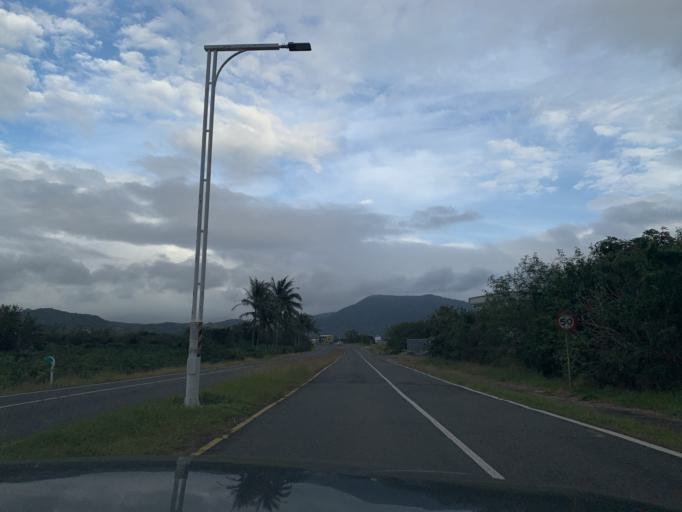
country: TW
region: Taiwan
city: Hengchun
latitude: 22.0522
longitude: 120.7169
